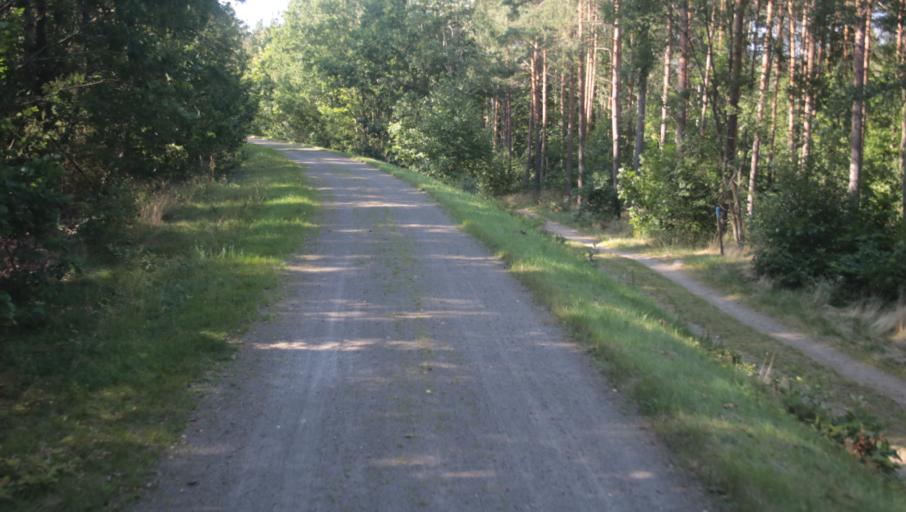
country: SE
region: Blekinge
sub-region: Karlshamns Kommun
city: Svangsta
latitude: 56.2853
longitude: 14.7523
